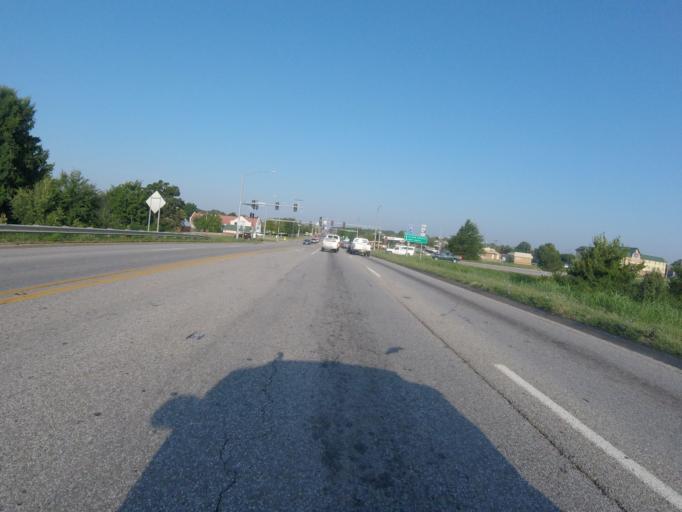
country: US
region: Arkansas
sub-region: Washington County
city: Fayetteville
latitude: 36.0783
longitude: -94.2014
